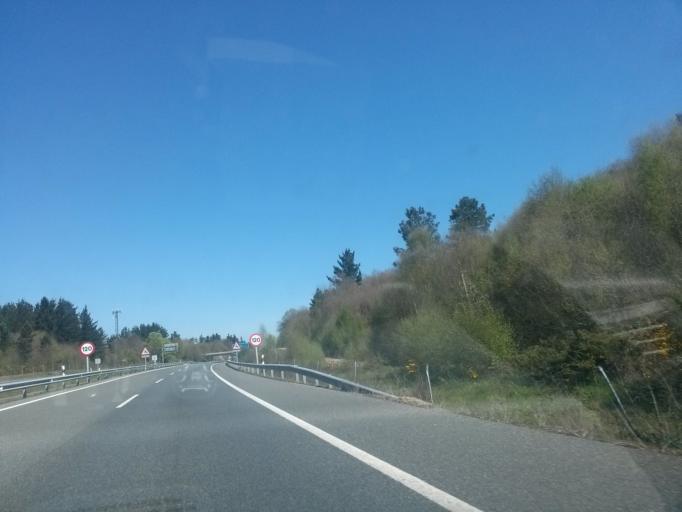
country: ES
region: Galicia
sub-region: Provincia de Lugo
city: Lugo
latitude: 43.0209
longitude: -7.5209
